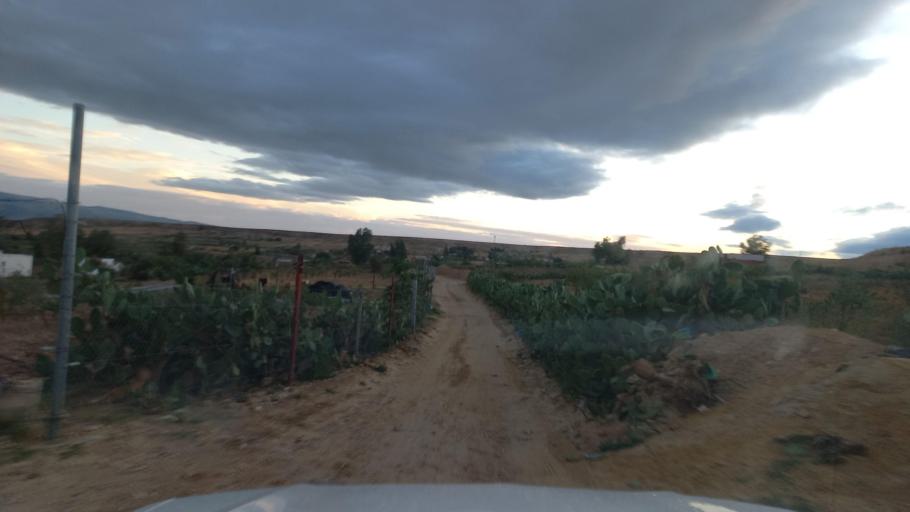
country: TN
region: Al Qasrayn
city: Kasserine
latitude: 35.2569
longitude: 8.9350
